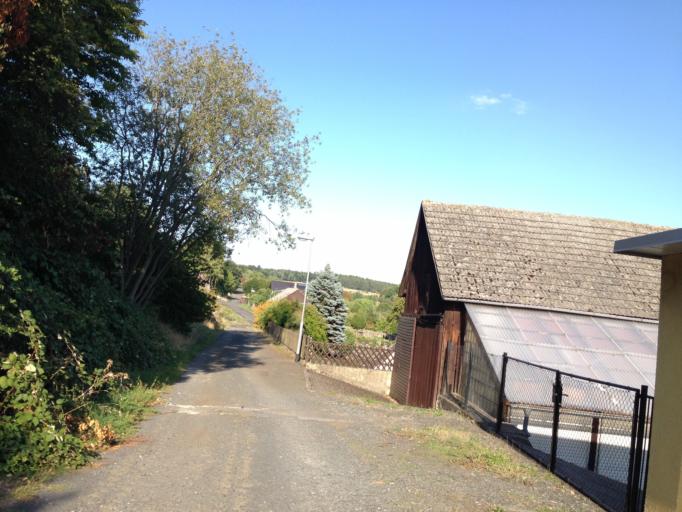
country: DE
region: Hesse
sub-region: Regierungsbezirk Giessen
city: Reiskirchen
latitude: 50.6186
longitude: 8.8502
